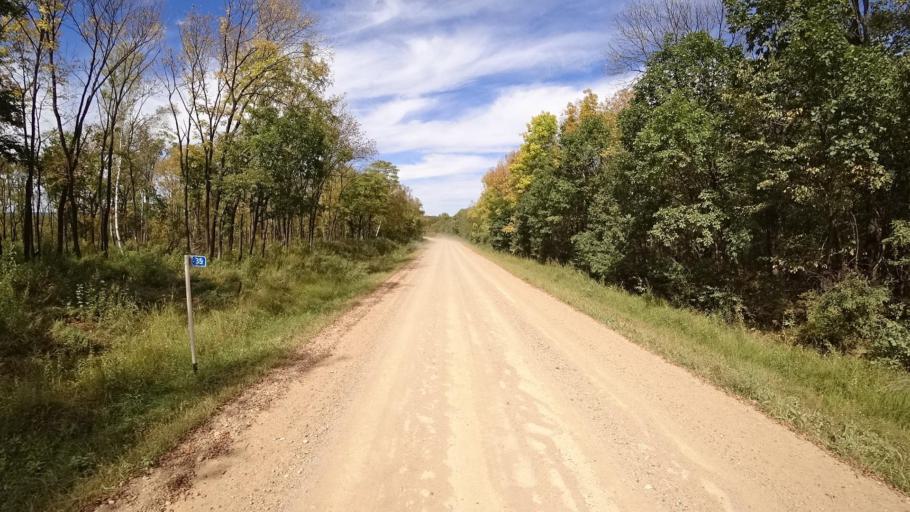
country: RU
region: Primorskiy
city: Yakovlevka
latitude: 44.6325
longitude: 133.6008
